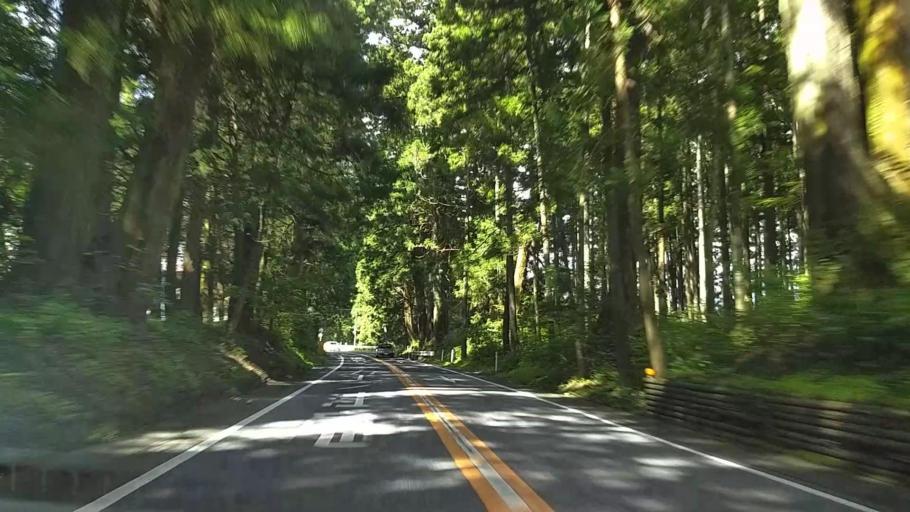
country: JP
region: Tochigi
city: Imaichi
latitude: 36.7126
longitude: 139.7351
